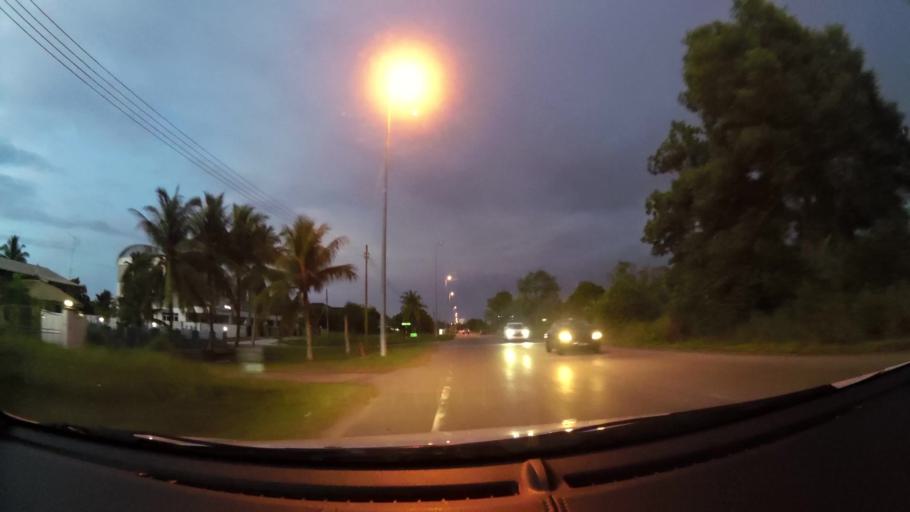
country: BN
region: Belait
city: Seria
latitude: 4.6514
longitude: 114.4229
